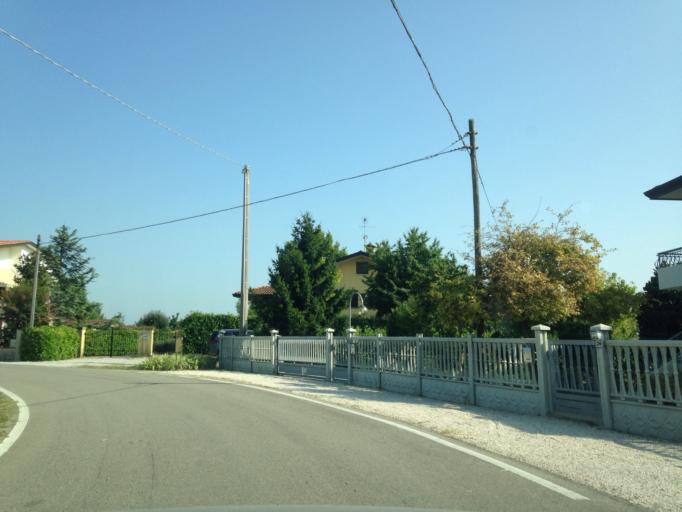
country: IT
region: Veneto
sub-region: Provincia di Venezia
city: Portogruaro
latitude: 45.7652
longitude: 12.8716
